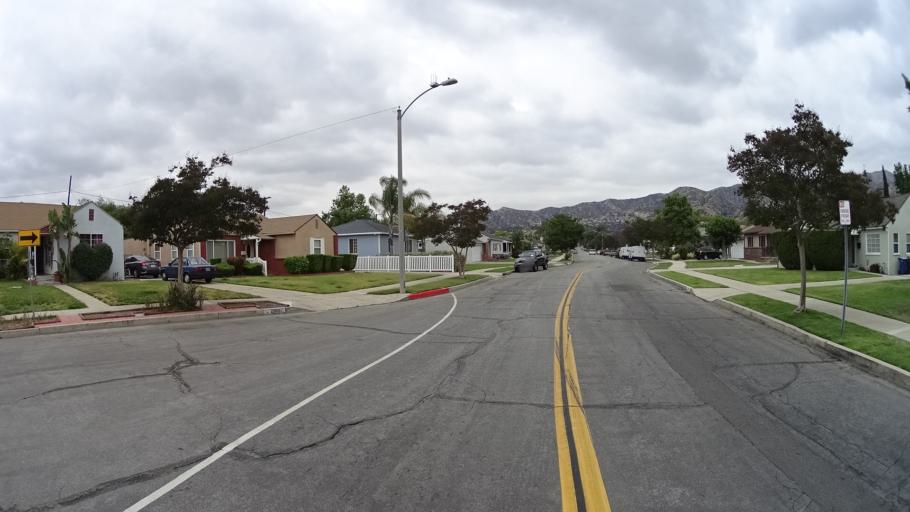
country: US
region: California
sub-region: Los Angeles County
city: Burbank
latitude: 34.1971
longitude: -118.3336
